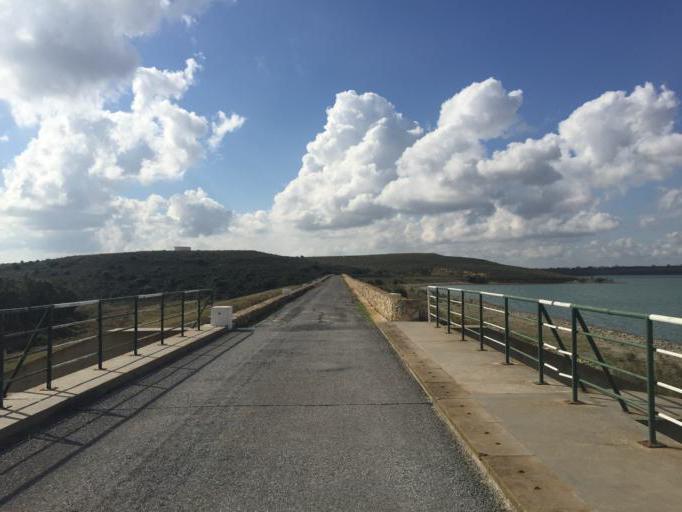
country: TN
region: Nabul
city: Menzel Heurr
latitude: 36.7391
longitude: 10.9221
